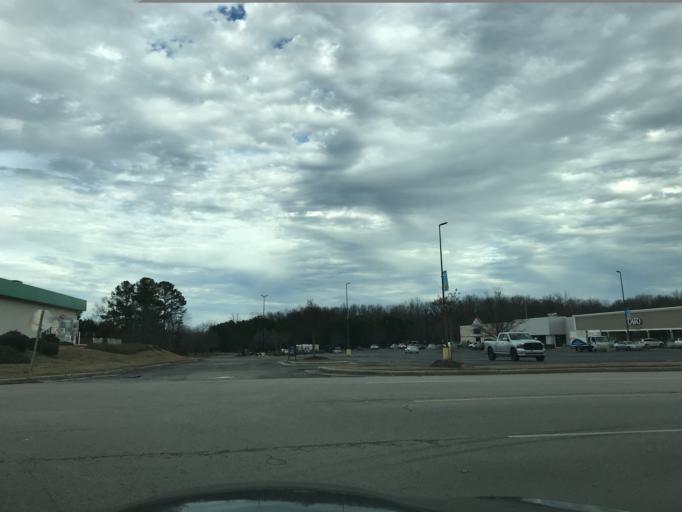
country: US
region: North Carolina
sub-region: Franklin County
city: Louisburg
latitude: 36.0896
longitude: -78.2999
